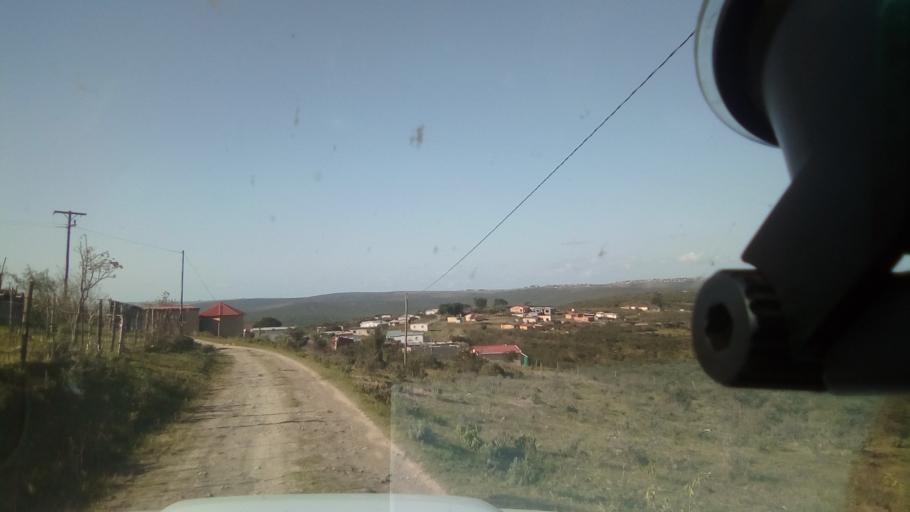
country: ZA
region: Eastern Cape
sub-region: Buffalo City Metropolitan Municipality
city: Bhisho
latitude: -32.7998
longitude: 27.3482
